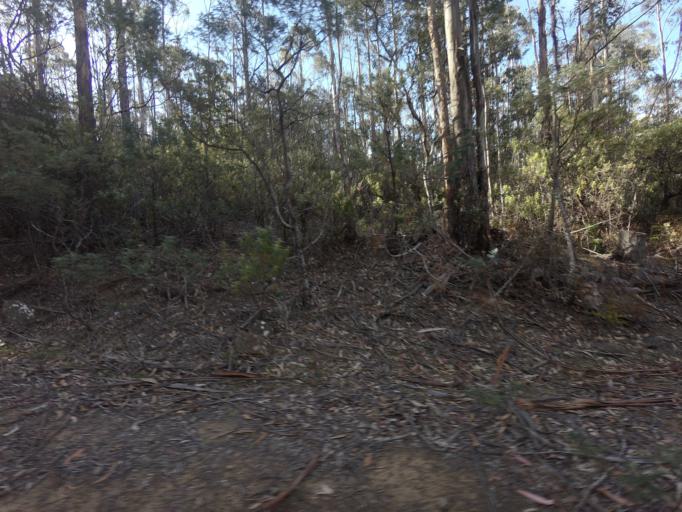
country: AU
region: Tasmania
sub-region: Break O'Day
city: St Helens
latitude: -41.8384
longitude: 148.0694
